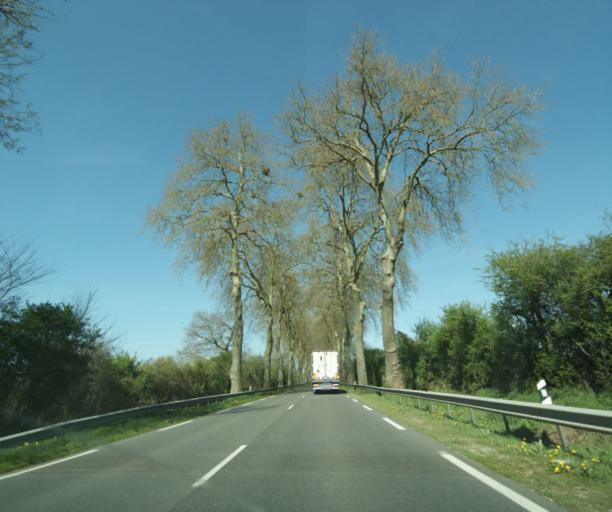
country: FR
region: Bourgogne
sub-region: Departement de la Nievre
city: Chantenay-Saint-Imbert
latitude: 46.7221
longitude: 3.1805
